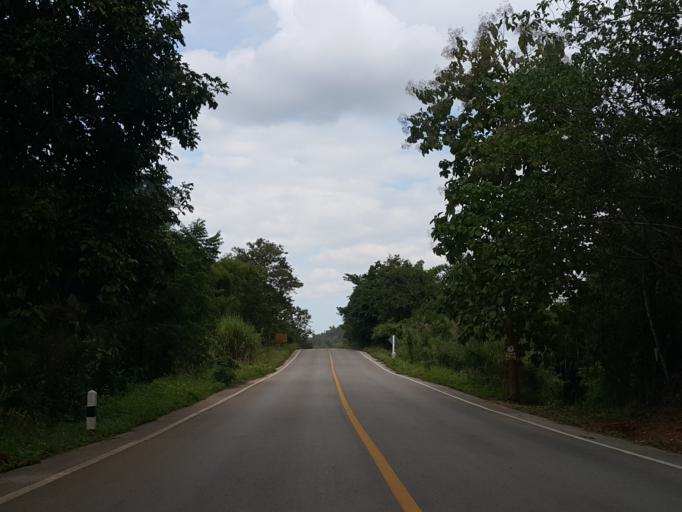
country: TH
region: Lampang
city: Chae Hom
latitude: 18.6305
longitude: 99.4908
